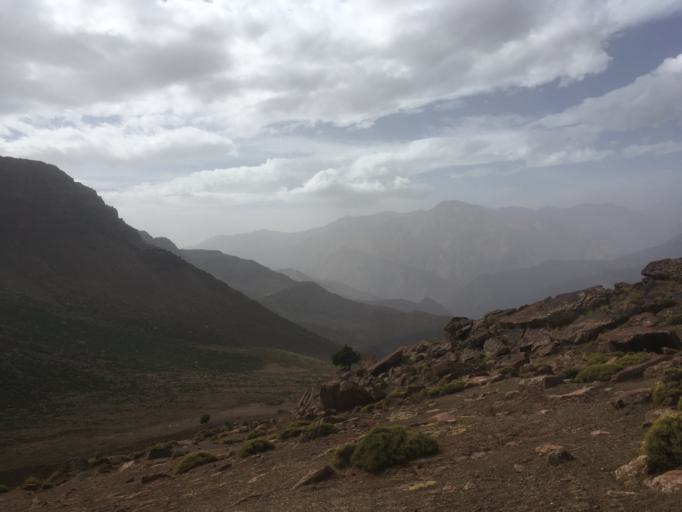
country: MA
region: Marrakech-Tensift-Al Haouz
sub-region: Al-Haouz
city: Tidili Mesfioua
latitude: 31.3236
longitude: -7.6702
